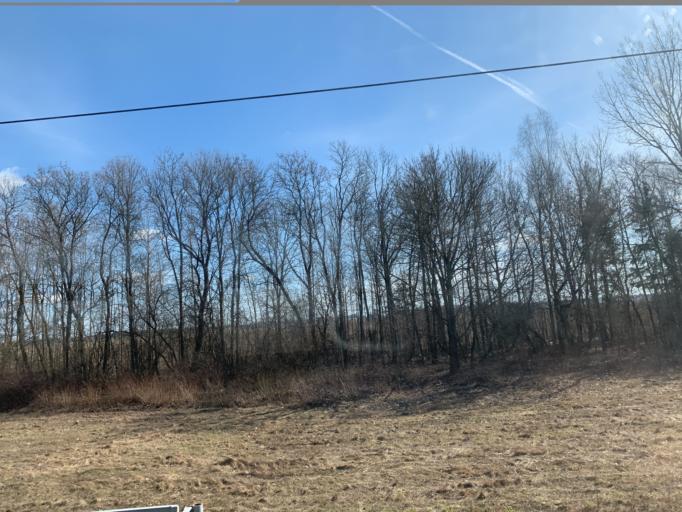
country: BY
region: Minsk
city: Haradzyeya
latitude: 53.3876
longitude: 26.6014
